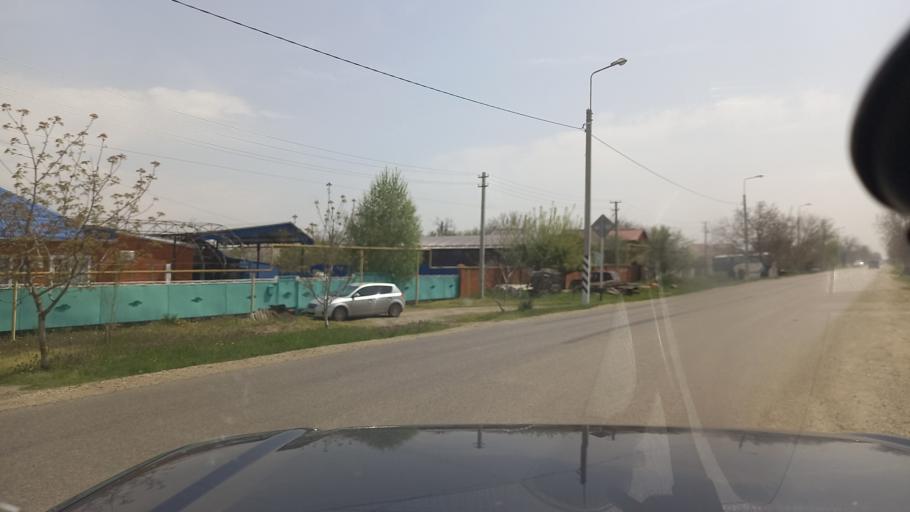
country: RU
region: Adygeya
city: Yablonovskiy
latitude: 44.9893
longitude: 38.9987
